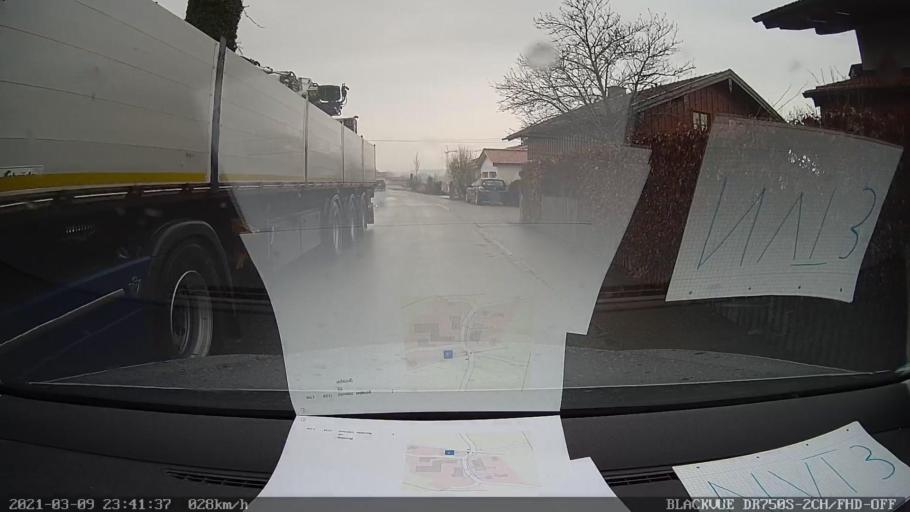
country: DE
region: Bavaria
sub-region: Upper Bavaria
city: Schonstett
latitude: 47.9802
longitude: 12.2384
